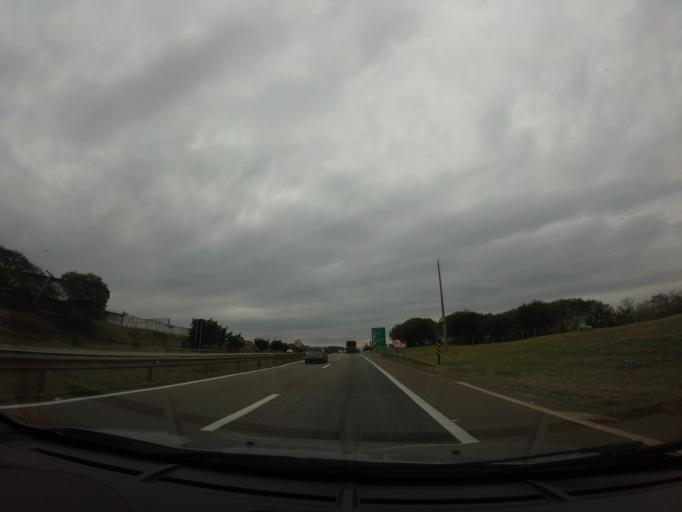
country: BR
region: Sao Paulo
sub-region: Piracicaba
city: Piracicaba
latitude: -22.7307
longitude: -47.6029
